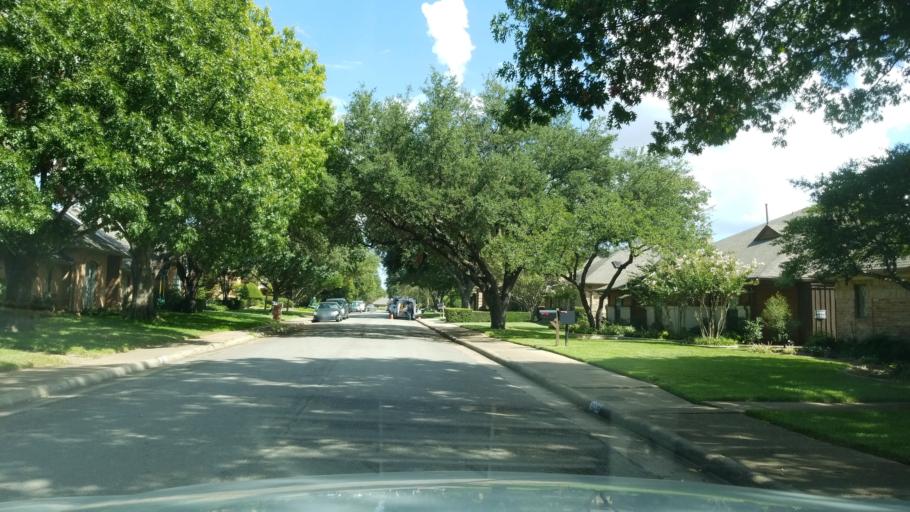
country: US
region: Texas
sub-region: Dallas County
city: Addison
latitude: 32.9605
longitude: -96.8012
